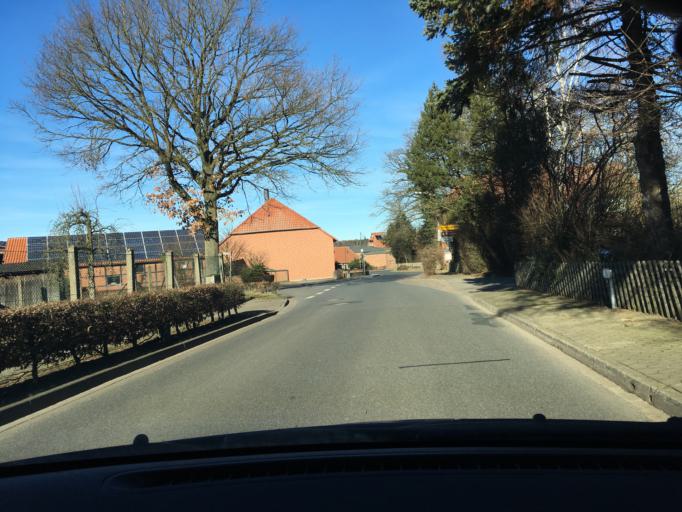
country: DE
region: Lower Saxony
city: Schwienau
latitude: 53.0042
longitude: 10.4452
